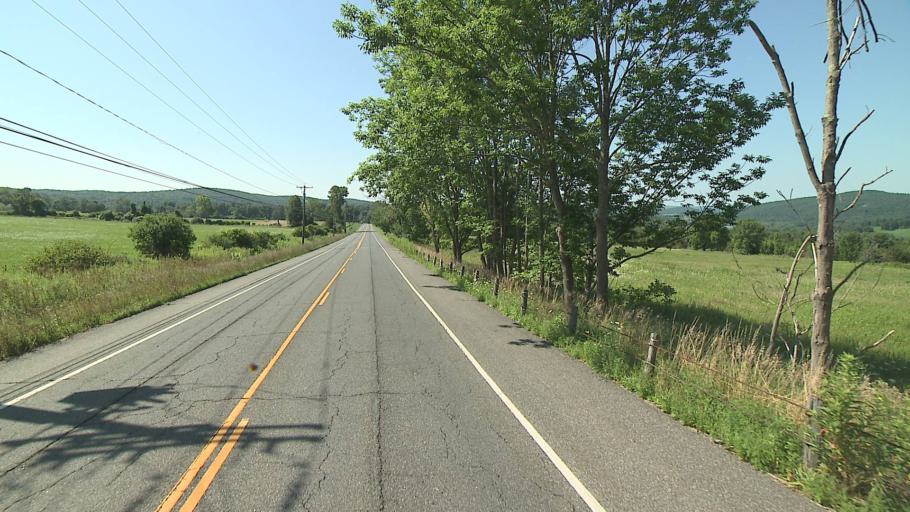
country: US
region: Connecticut
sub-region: Litchfield County
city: Canaan
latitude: 41.9231
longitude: -73.4443
